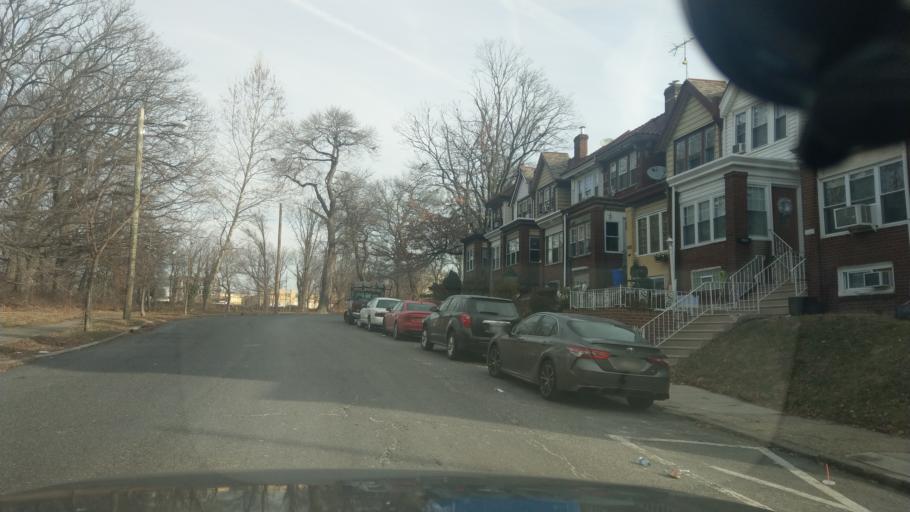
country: US
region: Pennsylvania
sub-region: Montgomery County
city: Jenkintown
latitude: 40.0422
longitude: -75.1306
